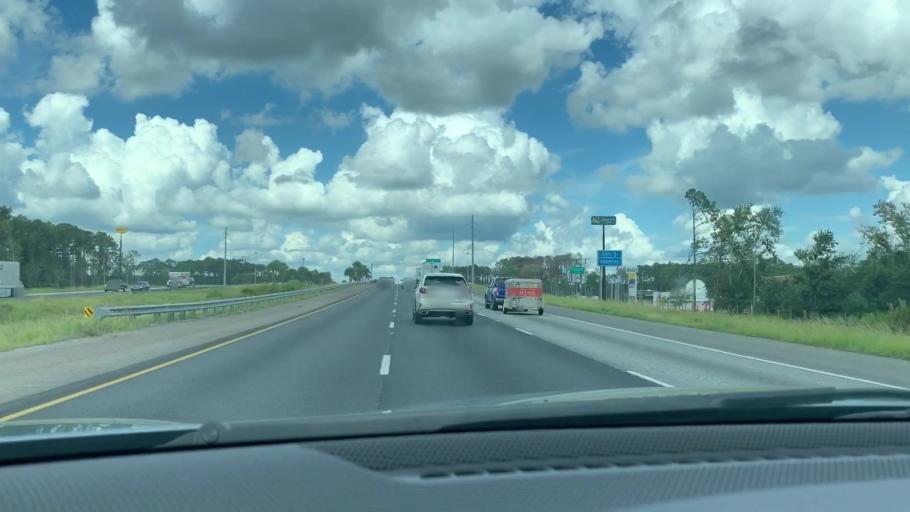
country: US
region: Georgia
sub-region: Camden County
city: Kingsland
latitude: 30.7871
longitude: -81.6579
